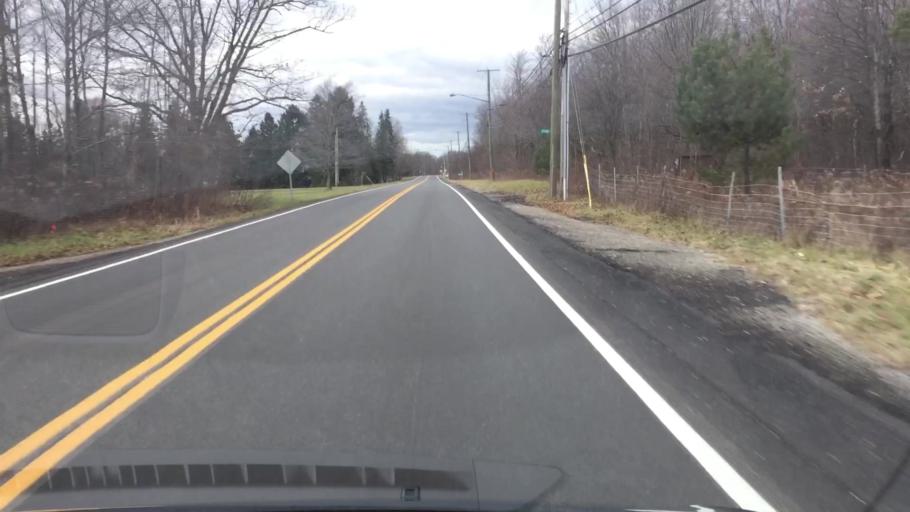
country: US
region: Ohio
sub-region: Summit County
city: Boston Heights
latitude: 41.2590
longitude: -81.5103
